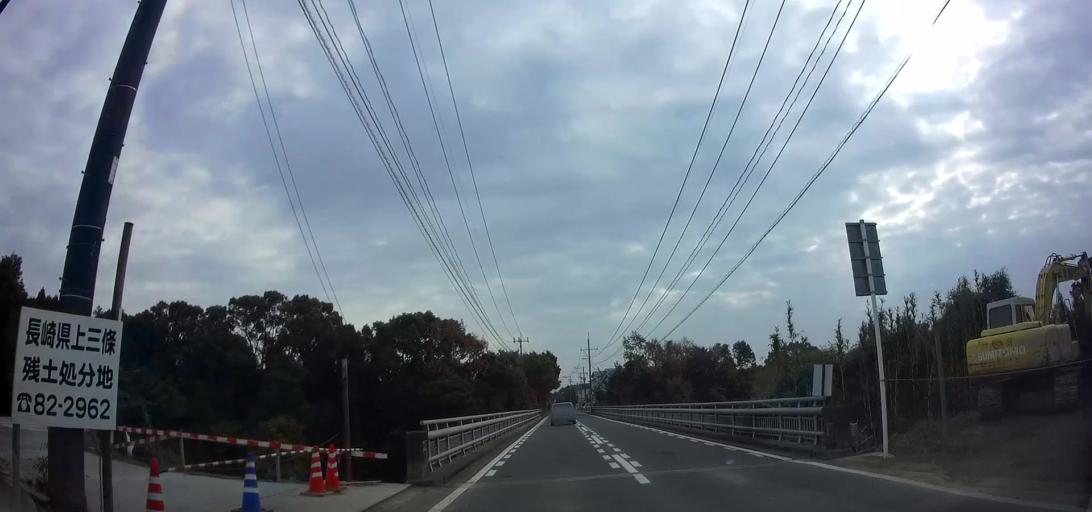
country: JP
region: Nagasaki
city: Shimabara
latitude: 32.6924
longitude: 130.3022
